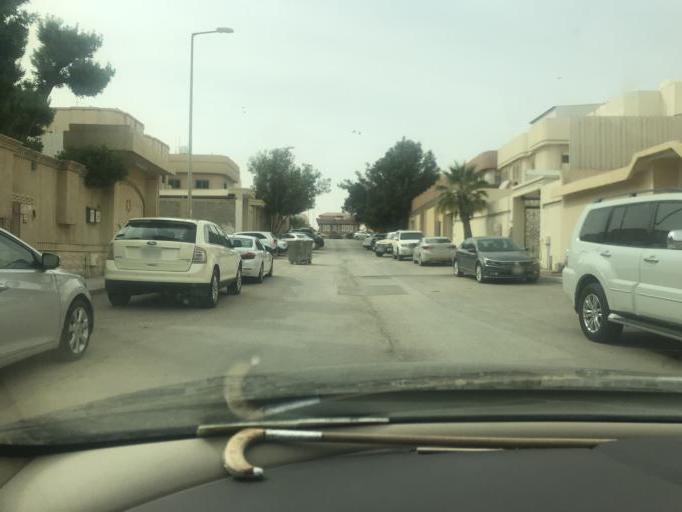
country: SA
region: Ar Riyad
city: Riyadh
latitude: 24.7501
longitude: 46.7625
